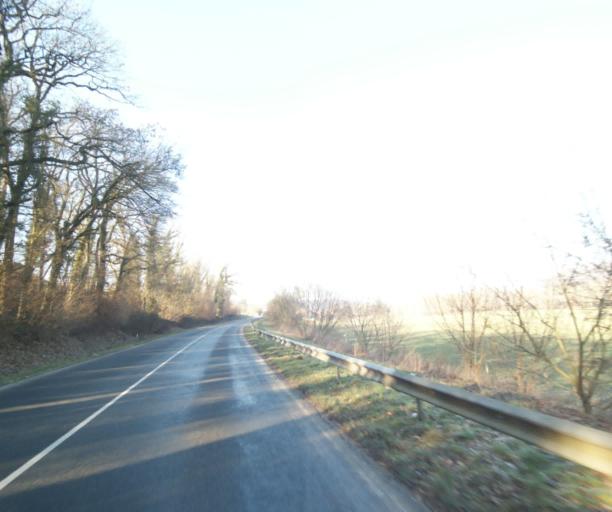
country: FR
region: Champagne-Ardenne
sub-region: Departement de la Haute-Marne
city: Chevillon
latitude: 48.5198
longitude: 5.1068
